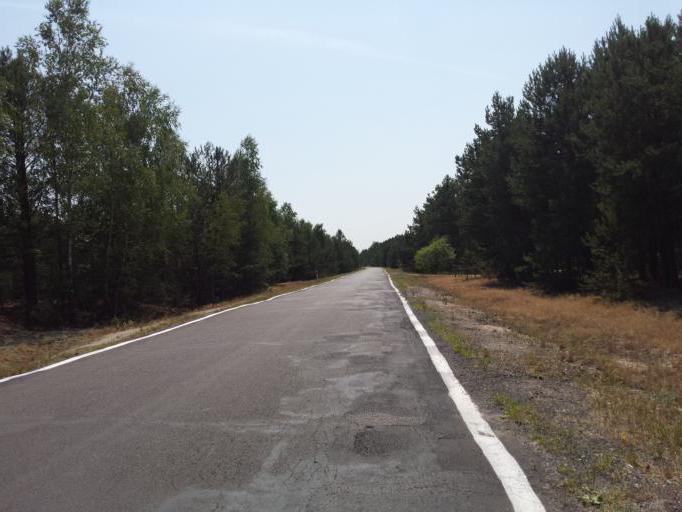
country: PL
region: Lublin Voivodeship
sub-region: Powiat bialski
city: Koden
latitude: 51.8917
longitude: 23.5968
